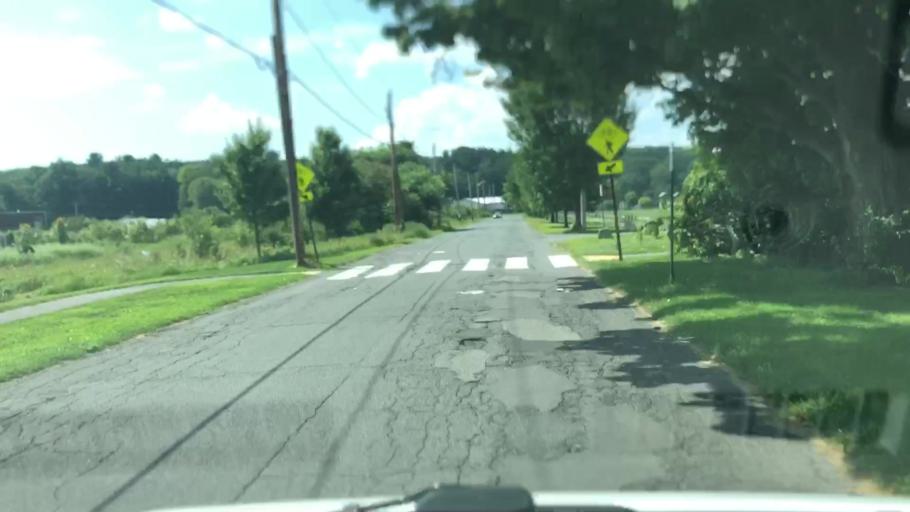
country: US
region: Massachusetts
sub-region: Hampshire County
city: Northampton
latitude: 42.3339
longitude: -72.6798
